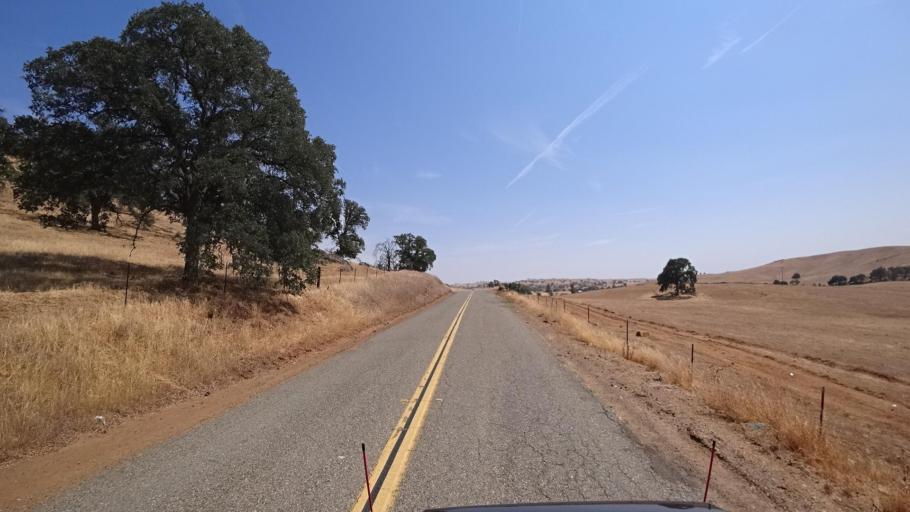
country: US
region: California
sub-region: Merced County
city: Planada
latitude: 37.5145
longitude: -120.2405
